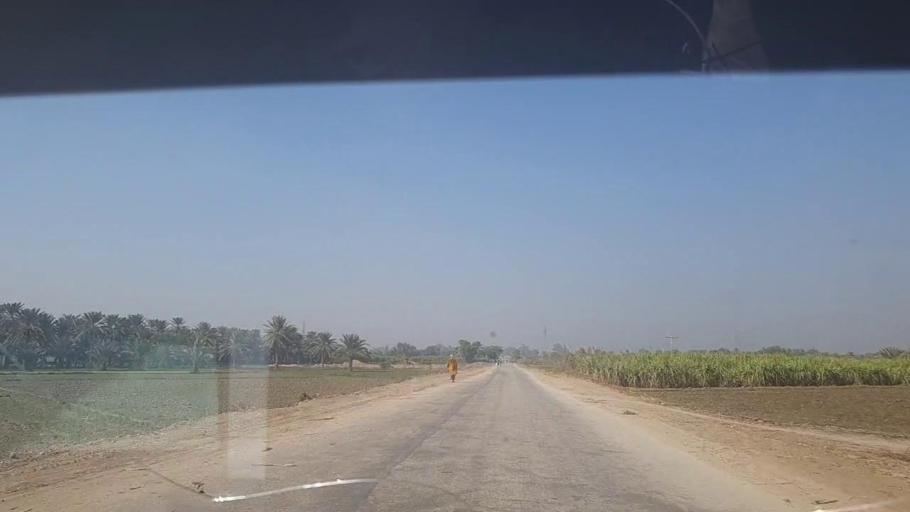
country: PK
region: Sindh
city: Kot Diji
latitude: 27.4245
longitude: 68.6576
